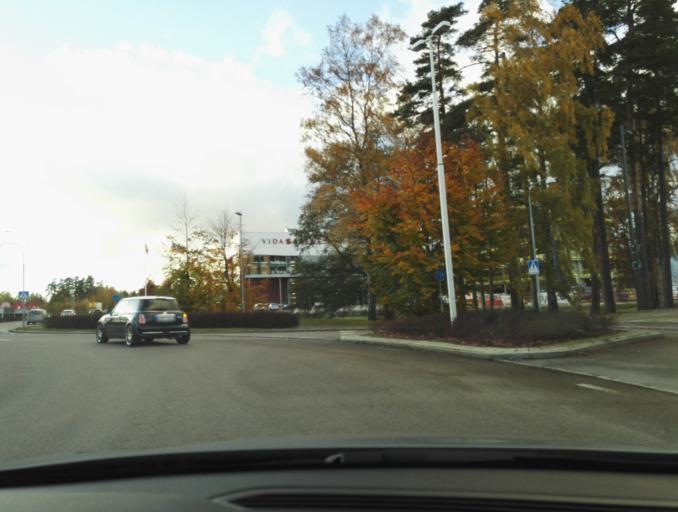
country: SE
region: Kronoberg
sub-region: Vaxjo Kommun
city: Vaexjoe
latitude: 56.8791
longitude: 14.7757
